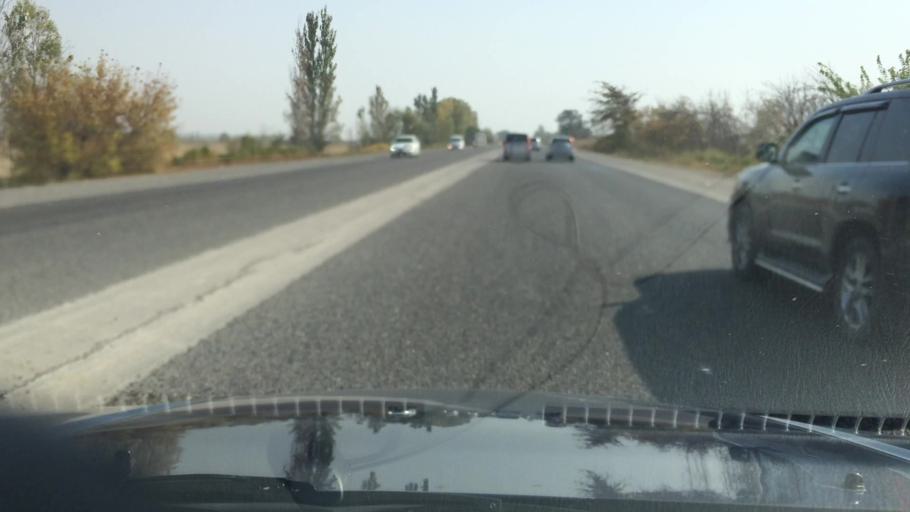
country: KG
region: Chuy
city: Kant
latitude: 42.9574
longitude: 74.9301
